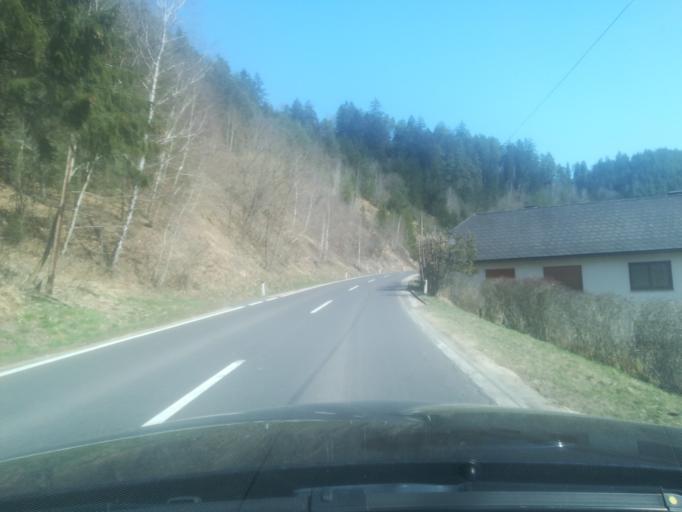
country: AT
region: Upper Austria
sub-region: Politischer Bezirk Freistadt
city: Freistadt
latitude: 48.4444
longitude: 14.5462
